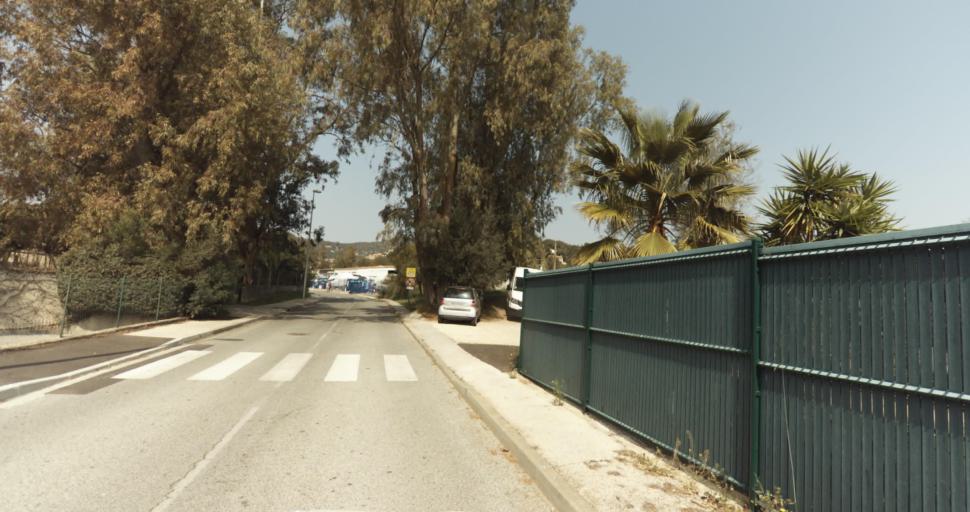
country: FR
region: Provence-Alpes-Cote d'Azur
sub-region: Departement du Var
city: Bormes-les-Mimosas
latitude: 43.1404
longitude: 6.3491
